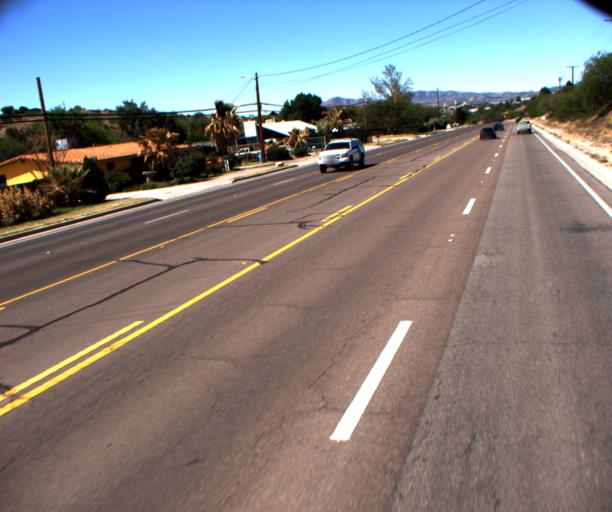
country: US
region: Arizona
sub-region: Santa Cruz County
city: Nogales
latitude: 31.3605
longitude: -110.9111
